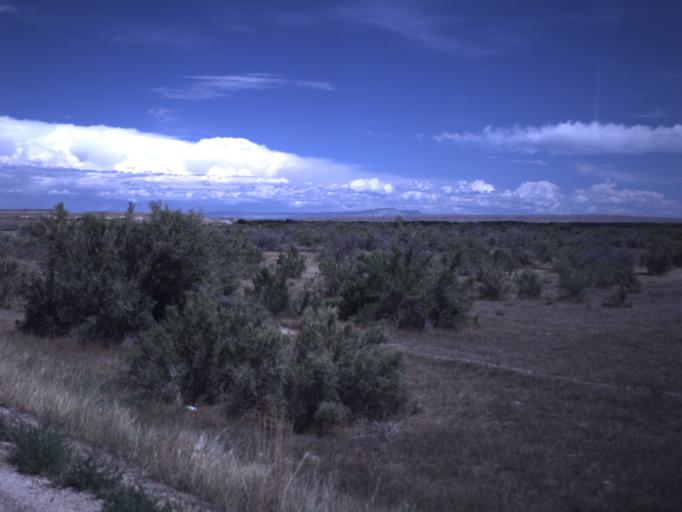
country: US
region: Utah
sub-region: Uintah County
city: Naples
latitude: 40.1202
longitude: -109.6655
